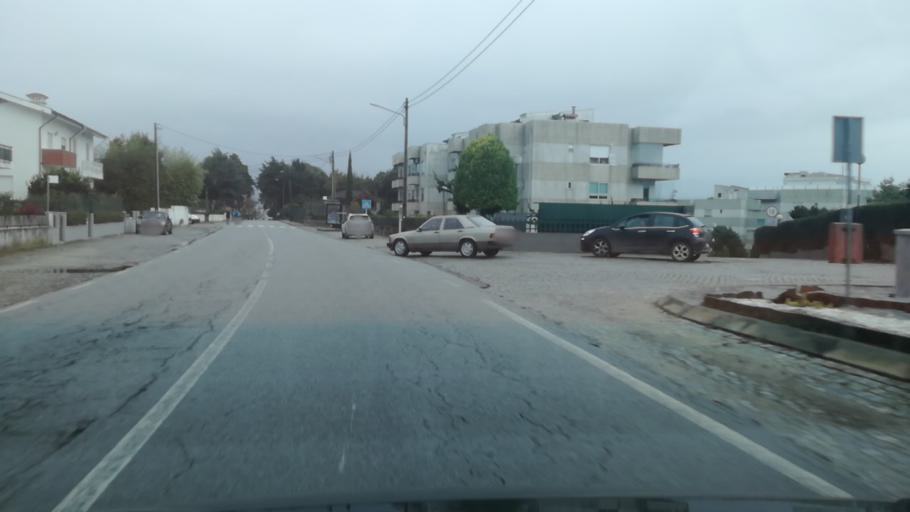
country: PT
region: Braga
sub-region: Braga
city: Braga
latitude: 41.5328
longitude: -8.4023
